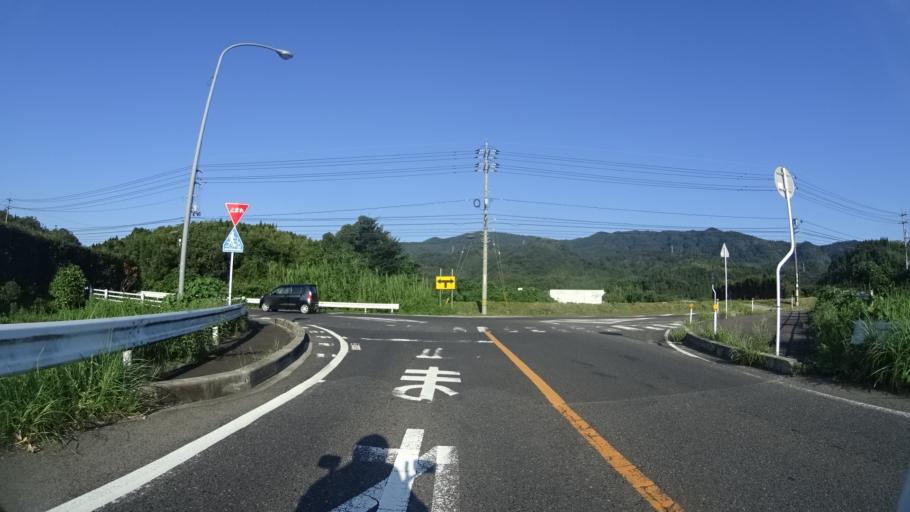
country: JP
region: Shimane
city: Sakaiminato
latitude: 35.5300
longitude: 133.1509
